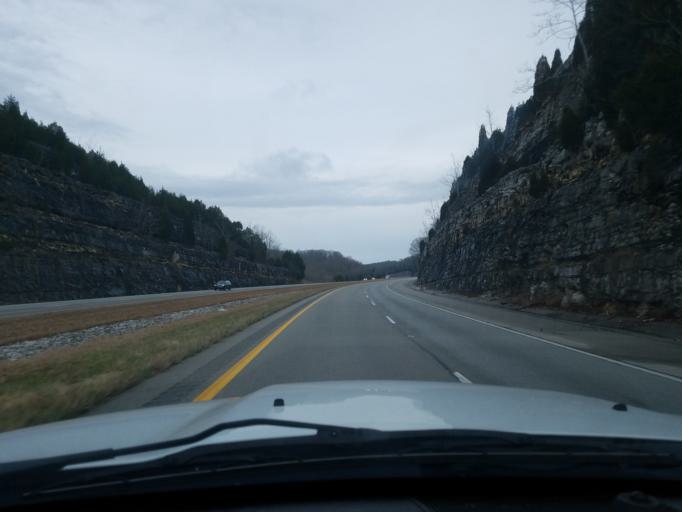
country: US
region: Indiana
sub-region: Harrison County
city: Corydon
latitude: 38.2351
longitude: -86.2382
